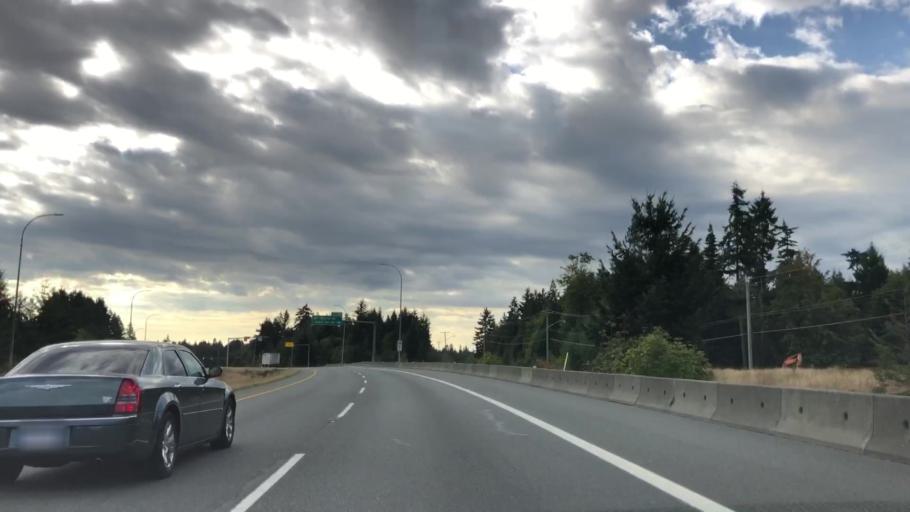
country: CA
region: British Columbia
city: Nanaimo
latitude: 49.2074
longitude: -124.0402
